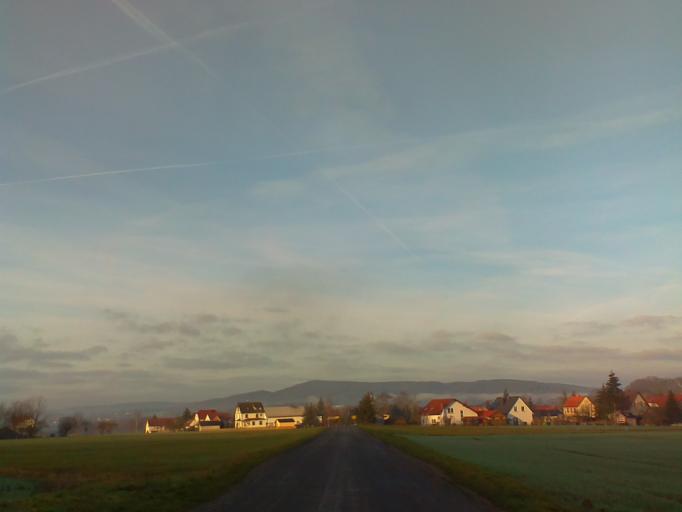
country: DE
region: Thuringia
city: Oppurg
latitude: 50.7094
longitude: 11.6382
